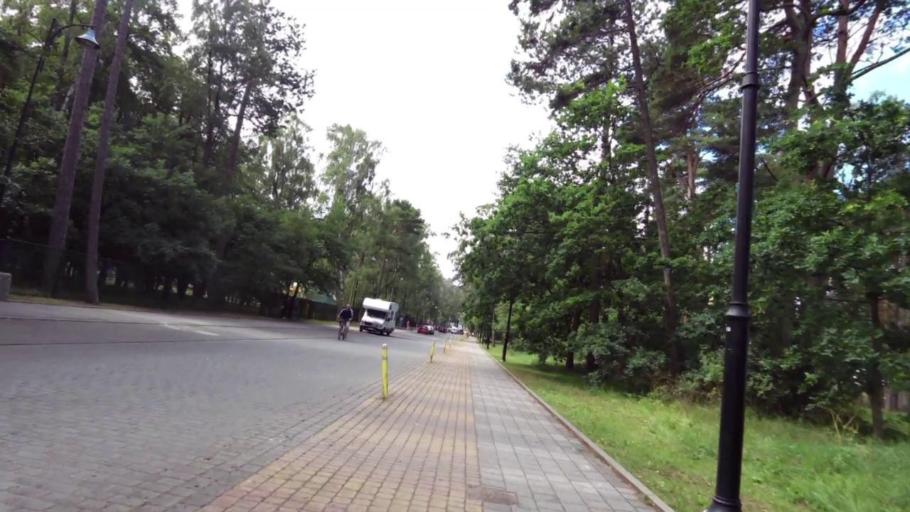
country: PL
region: West Pomeranian Voivodeship
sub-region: Powiat slawienski
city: Darlowo
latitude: 54.4433
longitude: 16.3911
